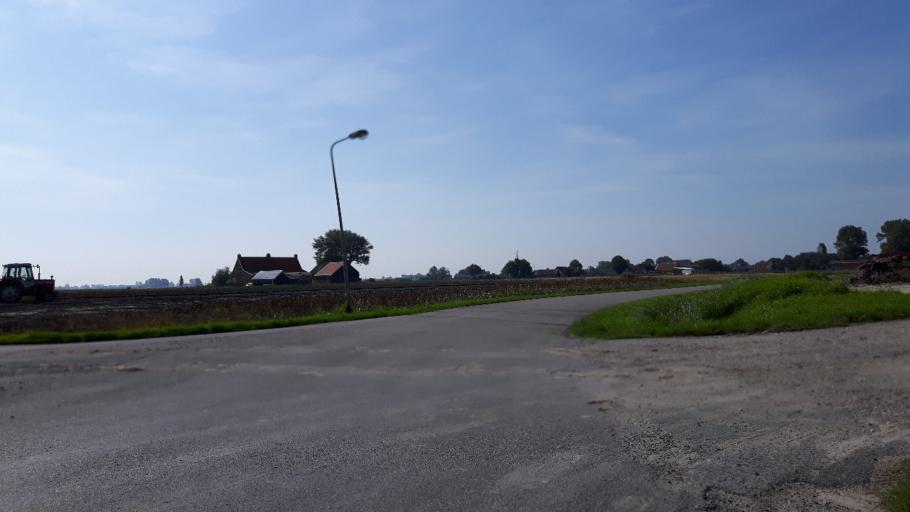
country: NL
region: Friesland
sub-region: Gemeente Dongeradeel
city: Holwerd
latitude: 53.3563
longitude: 5.8703
